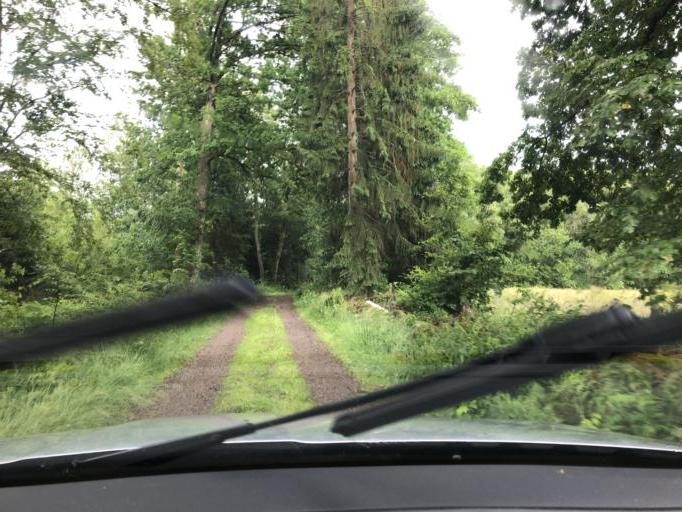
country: SE
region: Blekinge
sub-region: Solvesborgs Kommun
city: Soelvesborg
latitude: 56.1287
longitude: 14.5911
